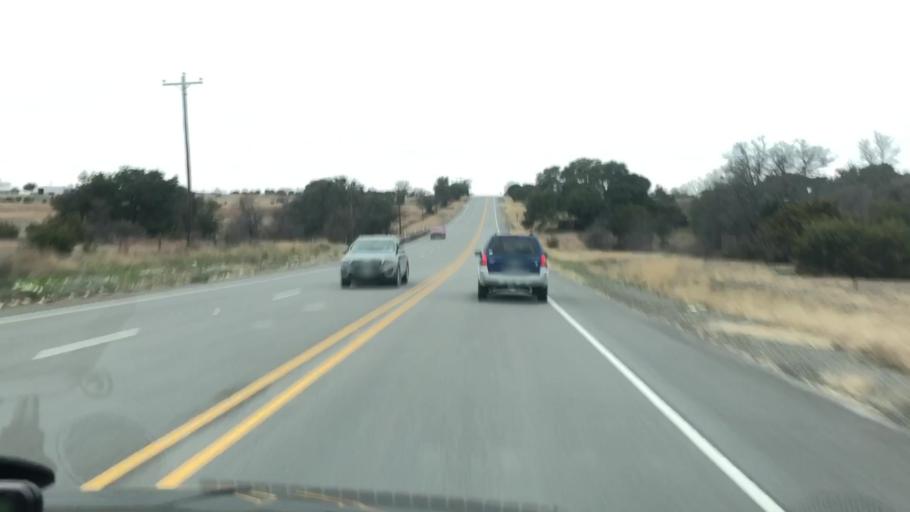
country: US
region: Texas
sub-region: Hamilton County
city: Hico
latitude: 32.0156
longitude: -98.0663
